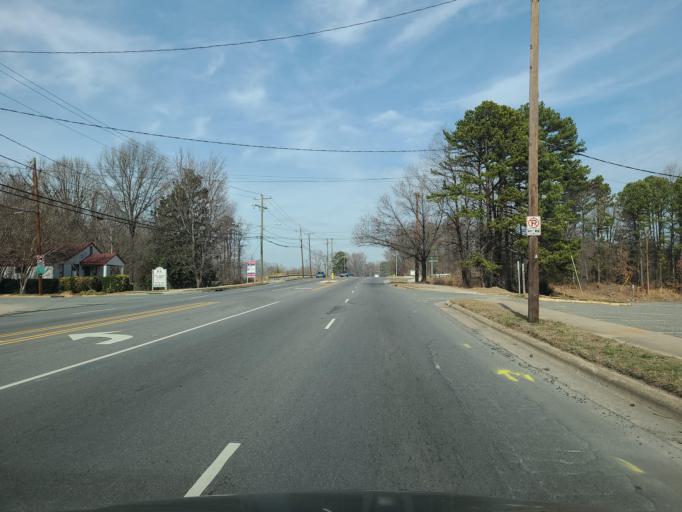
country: US
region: North Carolina
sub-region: Mecklenburg County
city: Charlotte
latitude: 35.2520
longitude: -80.7804
